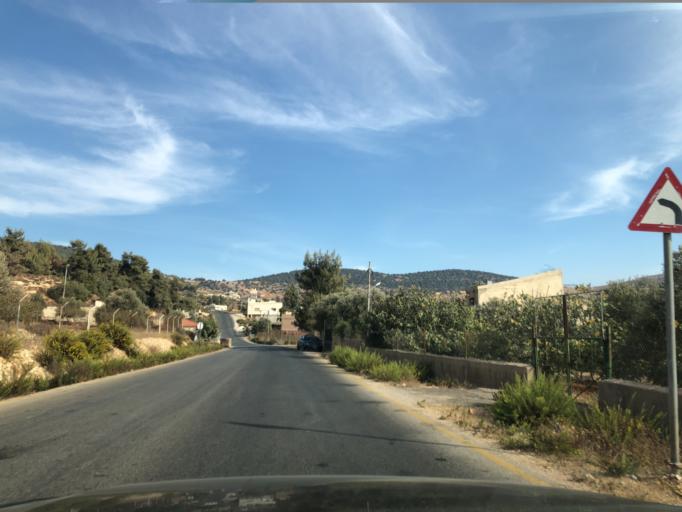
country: JO
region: Irbid
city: `Anjarah
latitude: 32.3182
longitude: 35.7660
